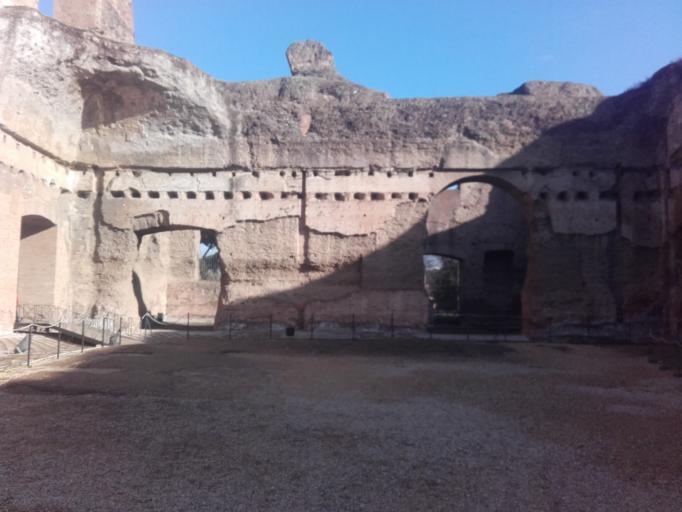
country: IT
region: Latium
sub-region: Citta metropolitana di Roma Capitale
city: Rome
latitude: 41.8789
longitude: 12.4938
